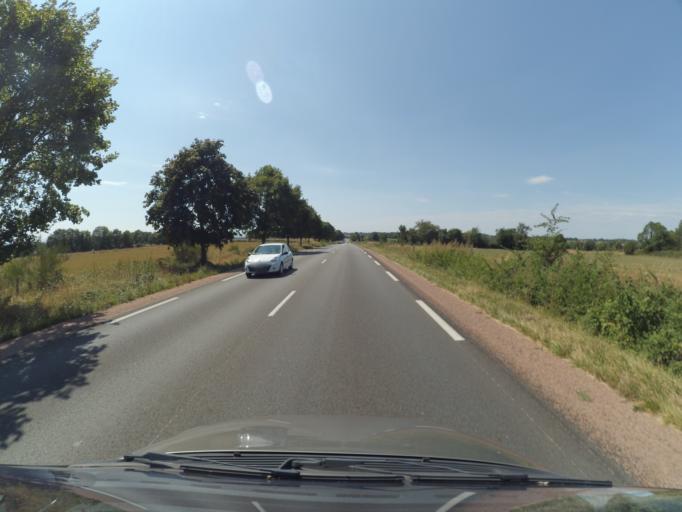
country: FR
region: Limousin
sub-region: Departement de la Haute-Vienne
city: Chateauponsac
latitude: 46.1940
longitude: 1.2658
